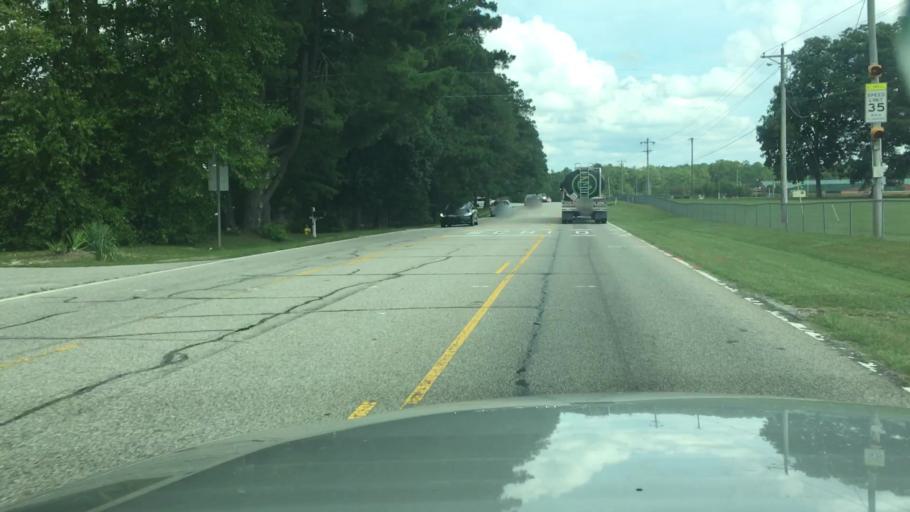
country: US
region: North Carolina
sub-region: Cumberland County
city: Hope Mills
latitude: 35.0028
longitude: -78.9923
